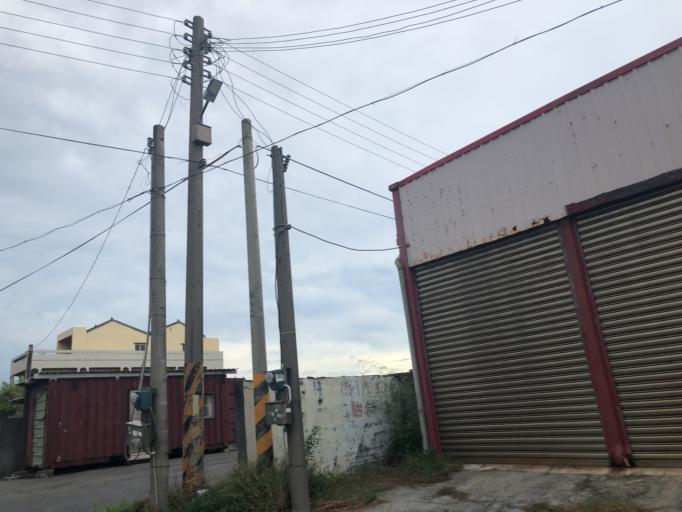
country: TW
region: Taiwan
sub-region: Chiayi
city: Taibao
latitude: 23.7072
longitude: 120.2005
